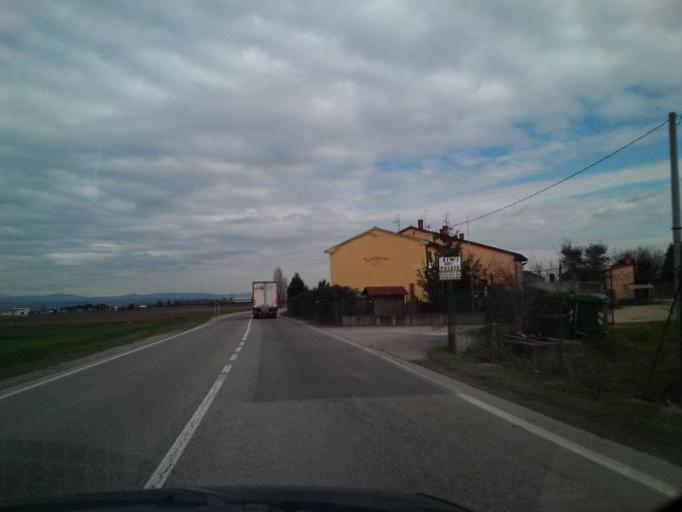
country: IT
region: Veneto
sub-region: Provincia di Verona
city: Sommacampagna
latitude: 45.4077
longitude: 10.8607
